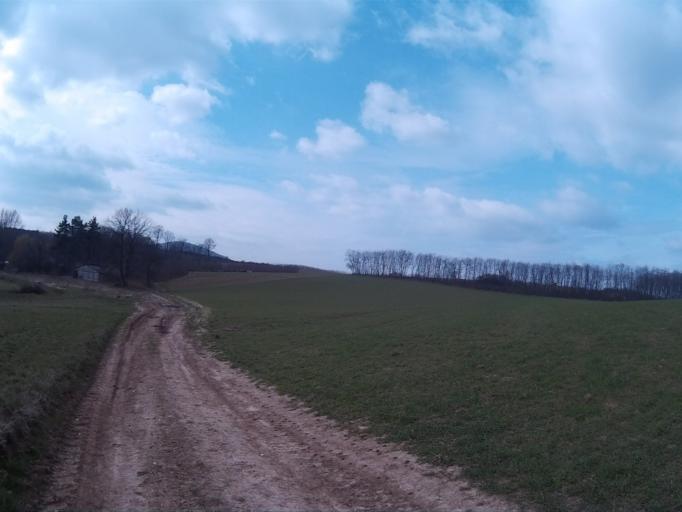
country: HU
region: Pest
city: Kosd
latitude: 47.8553
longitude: 19.1879
